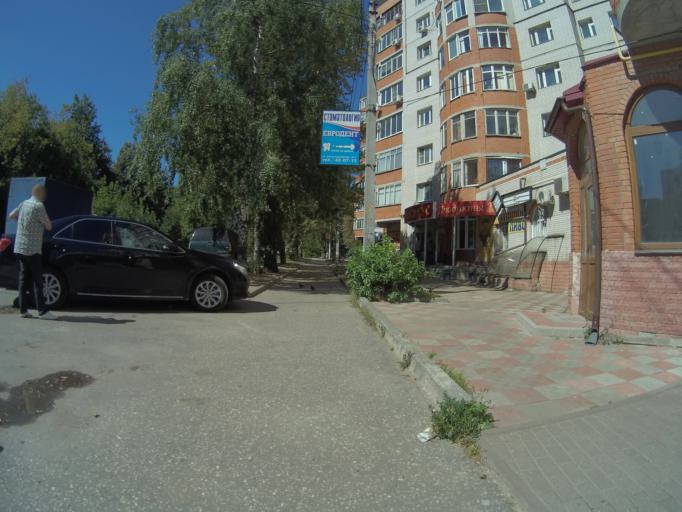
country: RU
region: Vladimir
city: Vladimir
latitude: 56.1292
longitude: 40.3723
